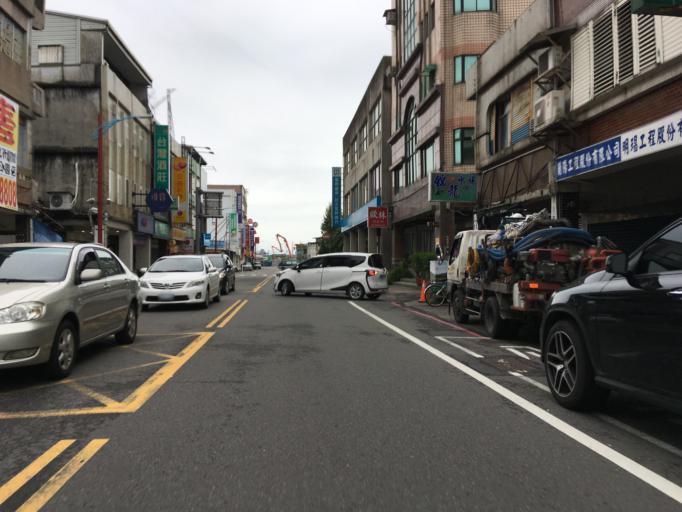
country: TW
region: Taiwan
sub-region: Yilan
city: Yilan
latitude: 24.6842
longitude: 121.7704
